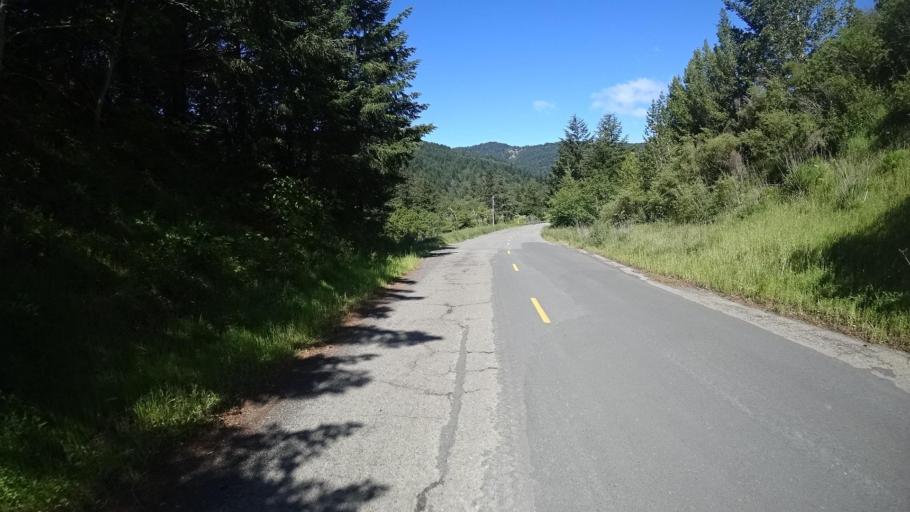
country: US
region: California
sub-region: Humboldt County
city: Rio Dell
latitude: 40.2760
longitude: -124.2415
